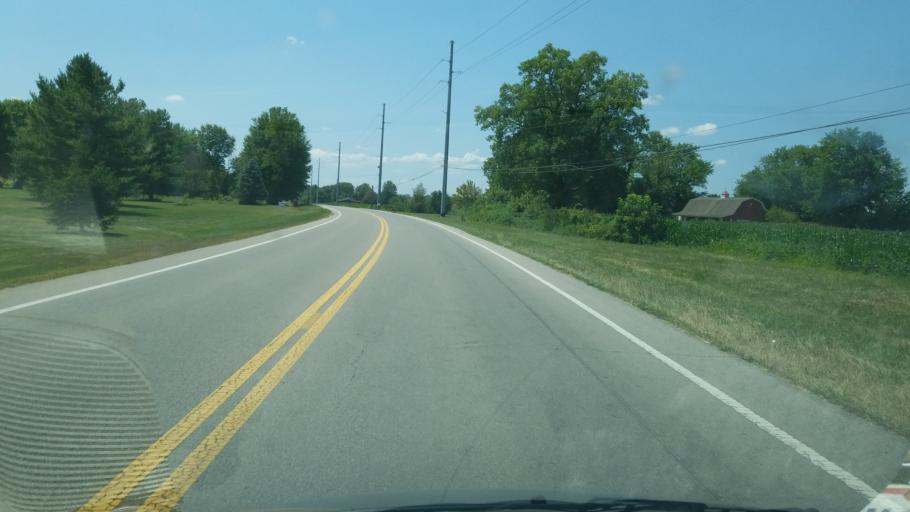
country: US
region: Ohio
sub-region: Franklin County
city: Lake Darby
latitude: 39.9738
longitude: -83.2036
